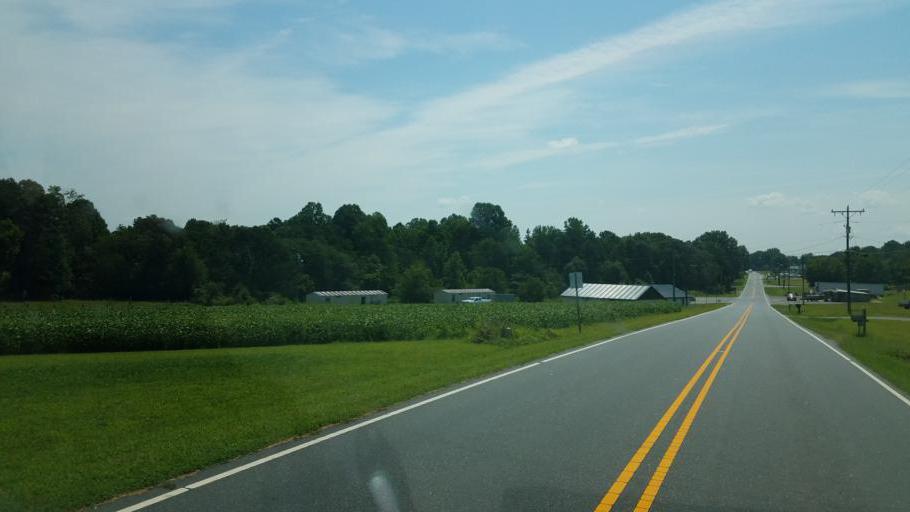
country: US
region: North Carolina
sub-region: Gaston County
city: Cherryville
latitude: 35.5117
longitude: -81.4631
